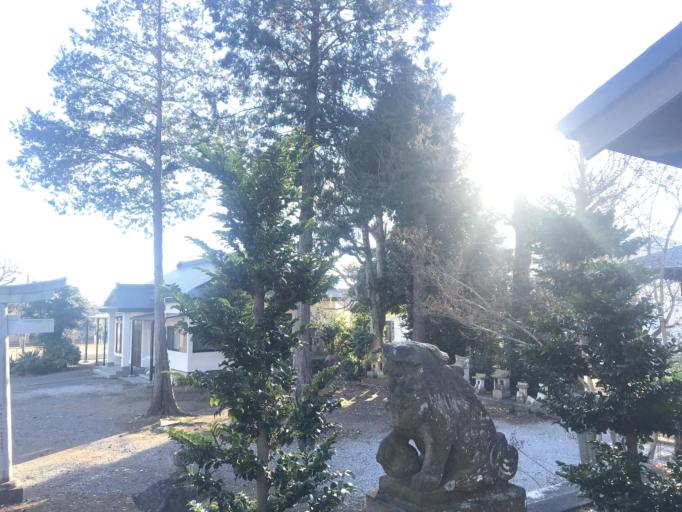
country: JP
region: Tochigi
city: Kaminokawa
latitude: 36.4360
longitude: 139.8704
